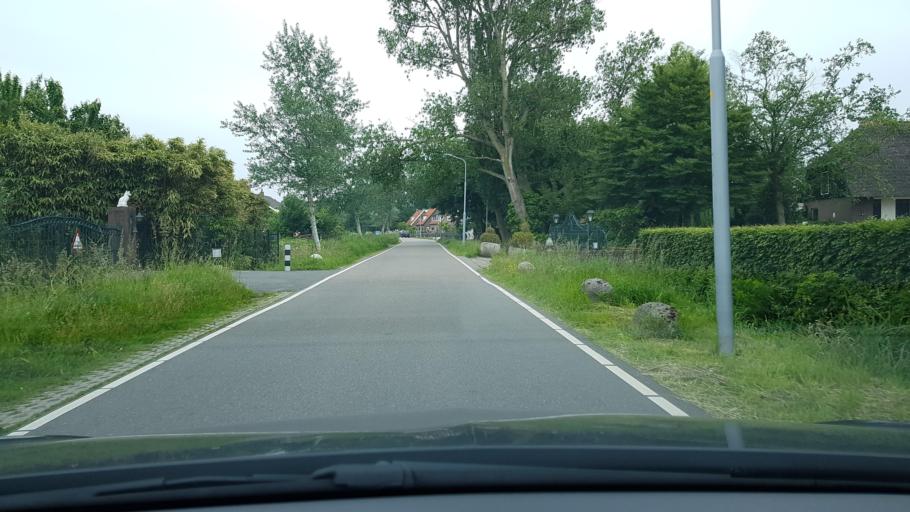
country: NL
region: North Holland
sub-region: Gemeente Haarlemmermeer
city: Hoofddorp
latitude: 52.3541
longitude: 4.7533
